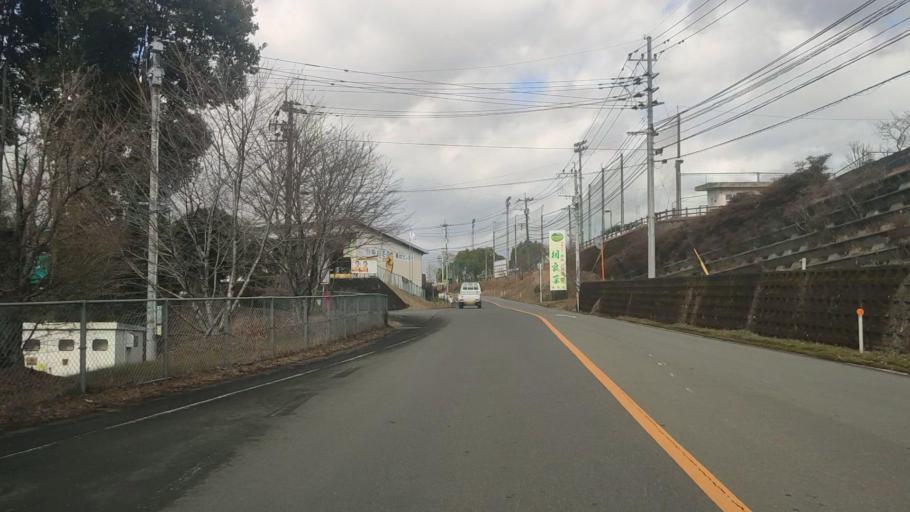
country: JP
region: Kumamoto
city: Hitoyoshi
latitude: 32.2351
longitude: 130.7953
